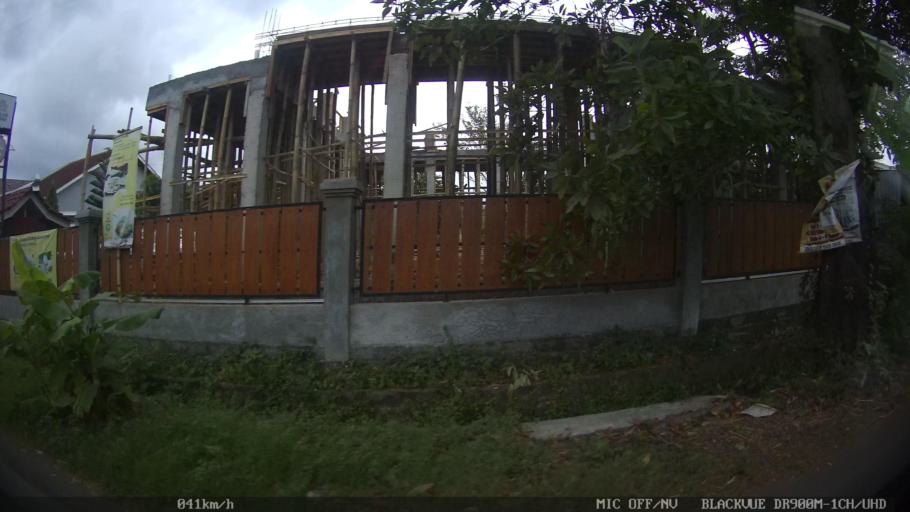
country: ID
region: Daerah Istimewa Yogyakarta
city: Depok
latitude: -7.8372
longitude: 110.4420
